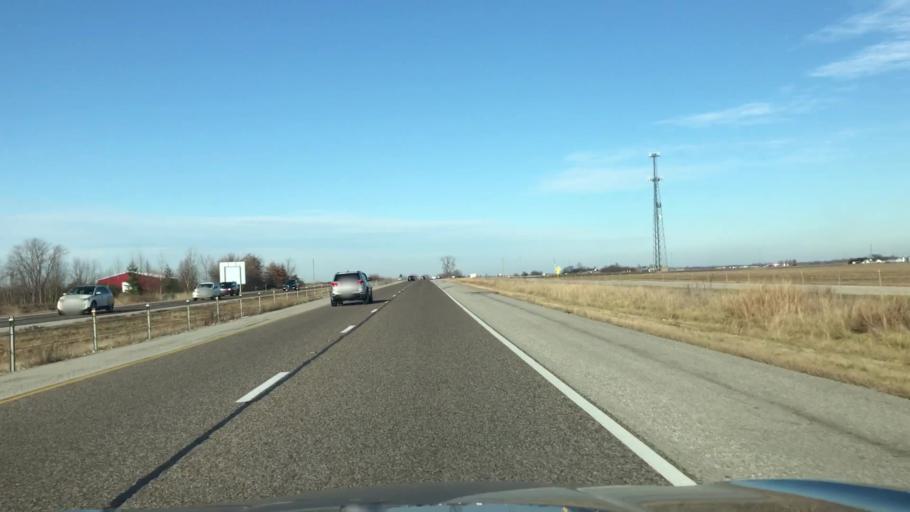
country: US
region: Illinois
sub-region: Madison County
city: Edwardsville
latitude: 38.8113
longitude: -89.8908
